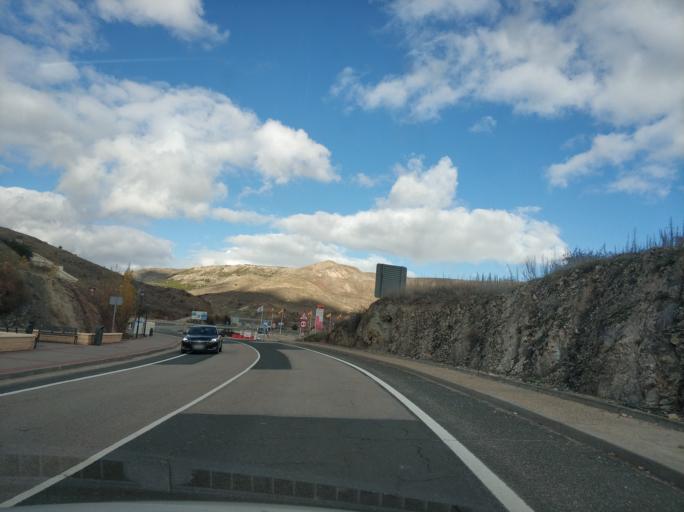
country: ES
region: Castille and Leon
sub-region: Provincia de Soria
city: Medinaceli
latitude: 41.1676
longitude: -2.4207
